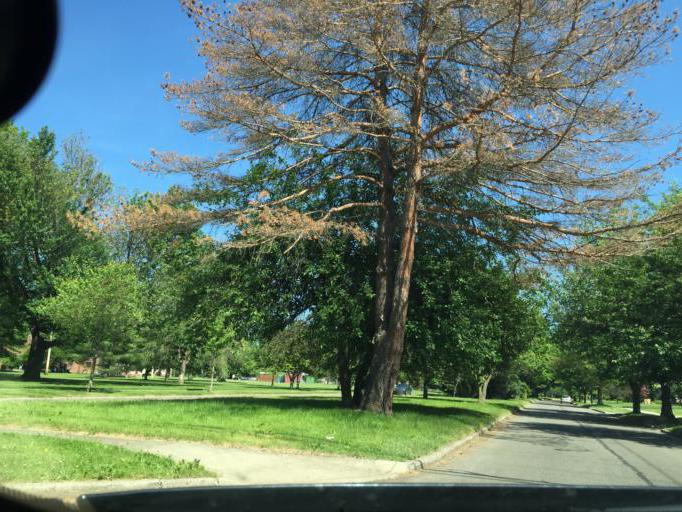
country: US
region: Michigan
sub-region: Oakland County
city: Southfield
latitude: 42.4065
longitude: -83.2254
